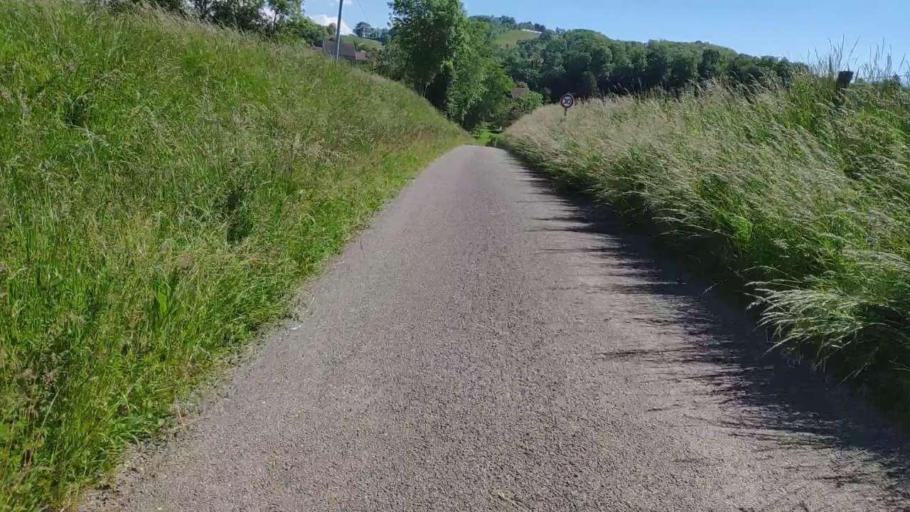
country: FR
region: Franche-Comte
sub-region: Departement du Jura
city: Perrigny
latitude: 46.7351
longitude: 5.5833
